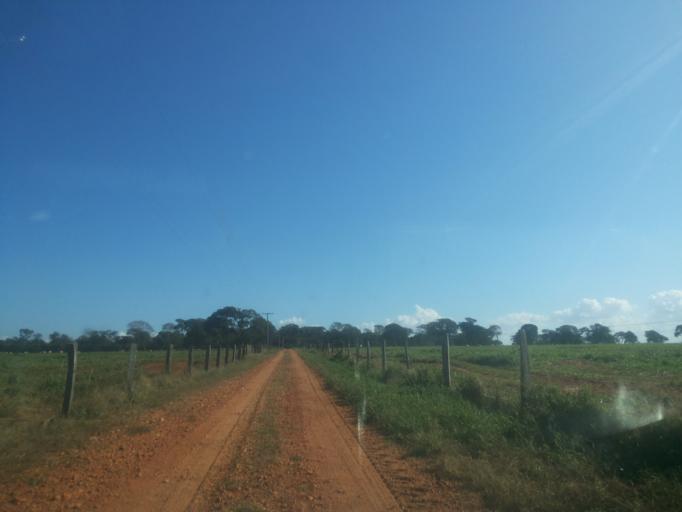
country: BR
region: Minas Gerais
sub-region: Santa Vitoria
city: Santa Vitoria
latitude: -19.0045
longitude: -50.3987
